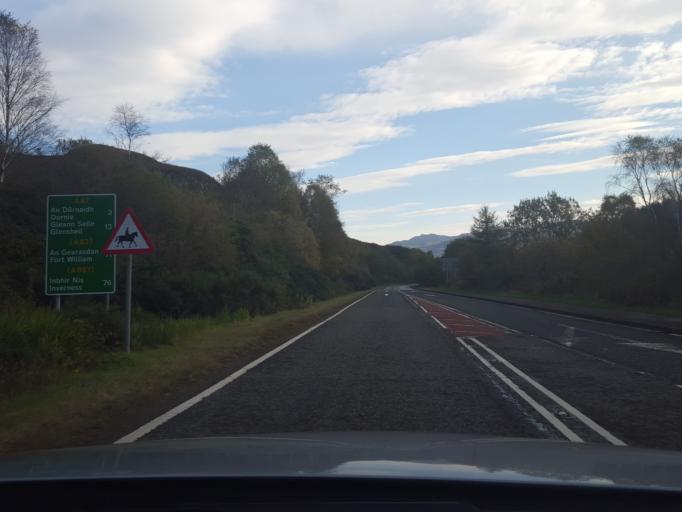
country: GB
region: Scotland
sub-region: Highland
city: Portree
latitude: 57.2855
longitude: -5.5802
